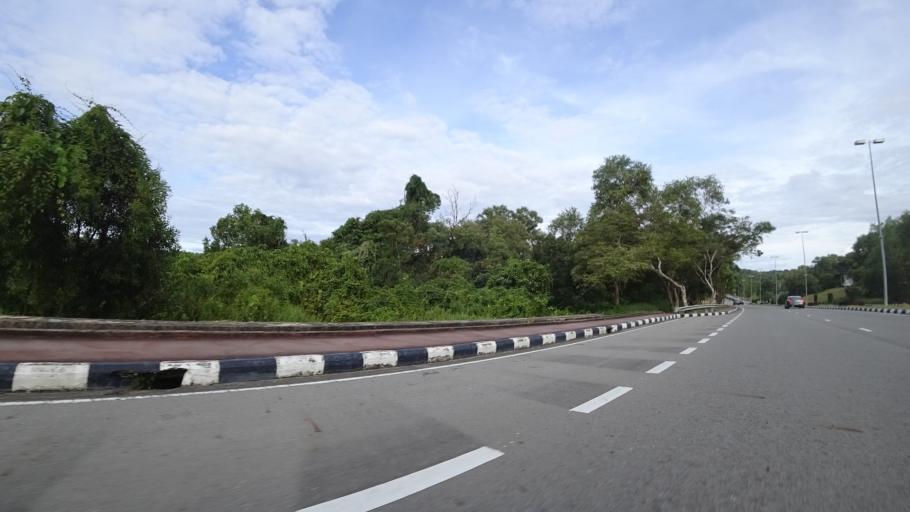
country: BN
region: Brunei and Muara
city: Bandar Seri Begawan
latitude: 4.9187
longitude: 114.9465
